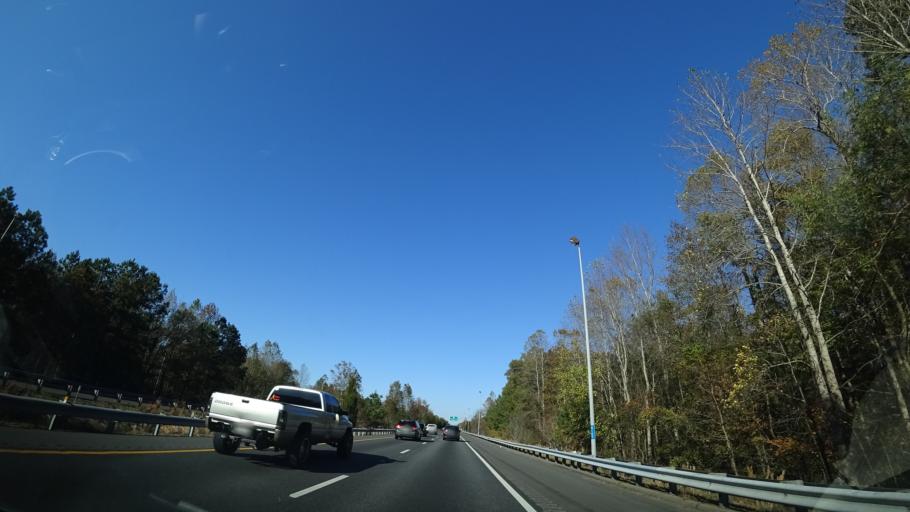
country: US
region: Virginia
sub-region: City of Portsmouth
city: Portsmouth Heights
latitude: 36.8353
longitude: -76.4335
